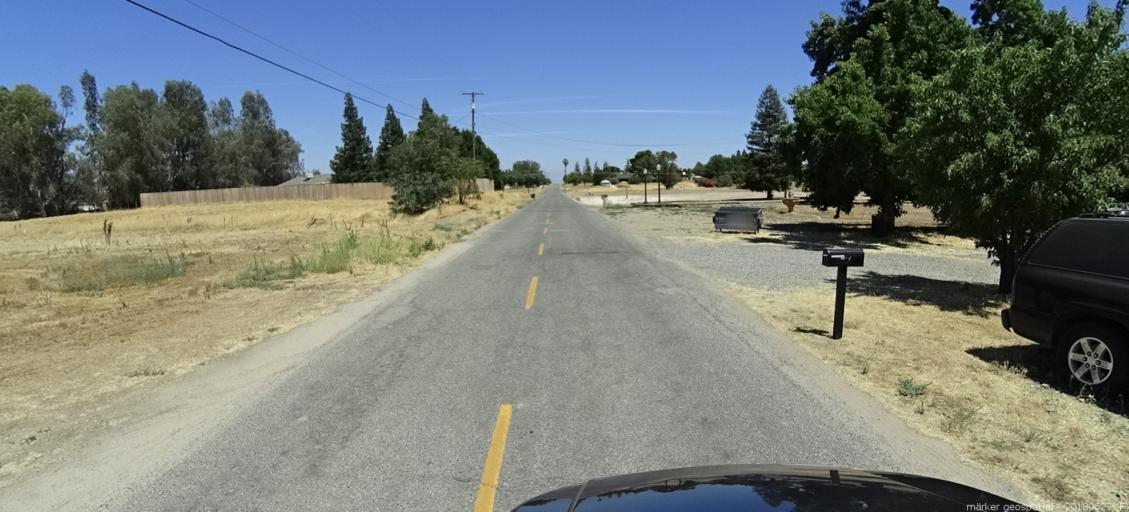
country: US
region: California
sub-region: Madera County
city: Bonadelle Ranchos-Madera Ranchos
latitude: 36.9618
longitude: -119.9051
